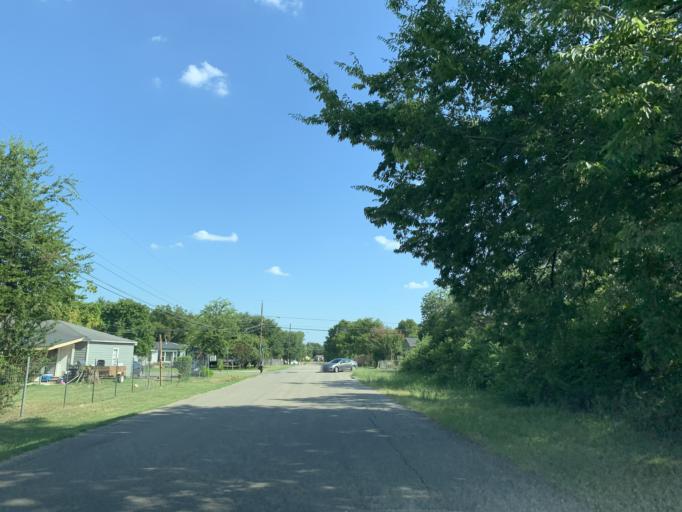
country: US
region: Texas
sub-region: Dallas County
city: Hutchins
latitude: 32.6566
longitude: -96.7697
